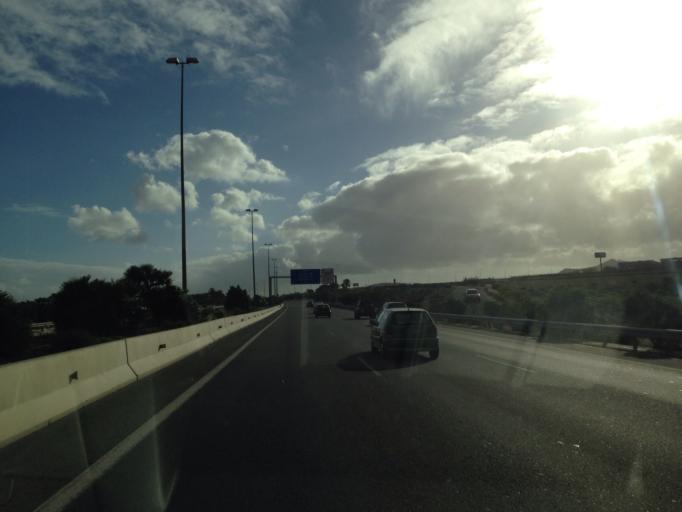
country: ES
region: Canary Islands
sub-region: Provincia de Las Palmas
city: Ingenio
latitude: 27.9284
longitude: -15.3962
